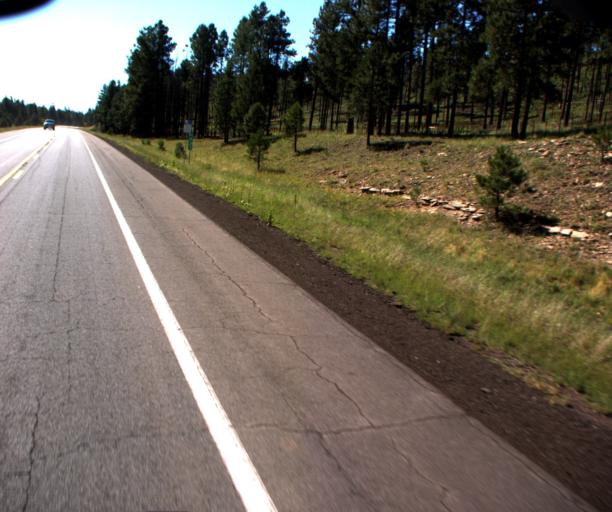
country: US
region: New Mexico
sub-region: Catron County
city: Reserve
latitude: 33.8231
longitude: -109.0787
